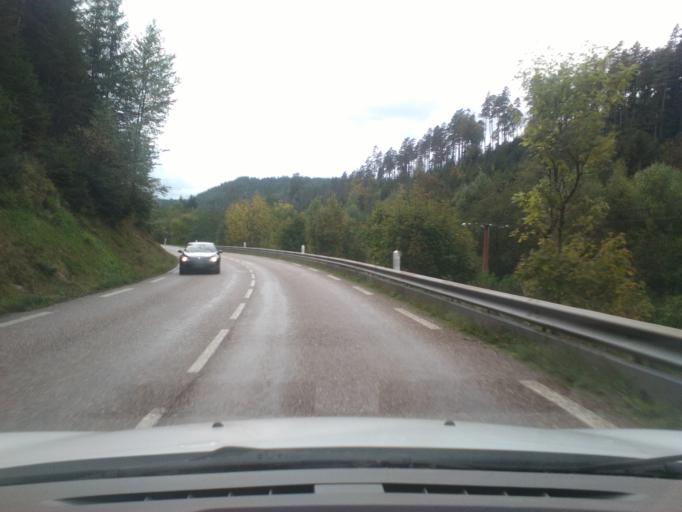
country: FR
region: Lorraine
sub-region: Departement des Vosges
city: Taintrux
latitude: 48.2713
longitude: 6.8302
